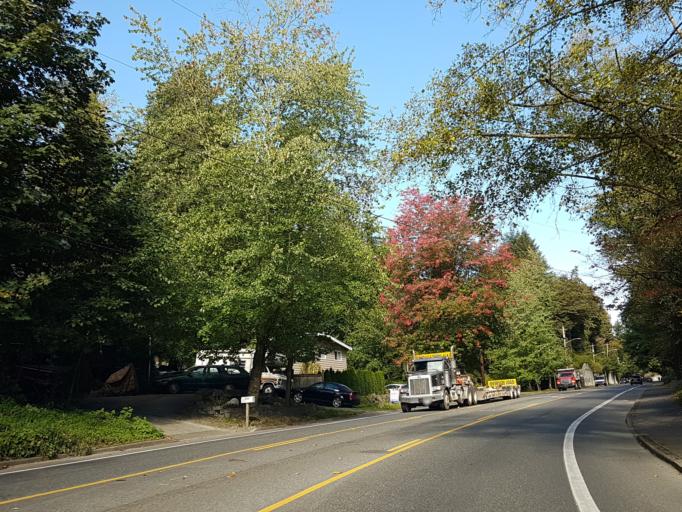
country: US
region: Washington
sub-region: King County
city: Lake Forest Park
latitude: 47.7619
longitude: -122.2638
